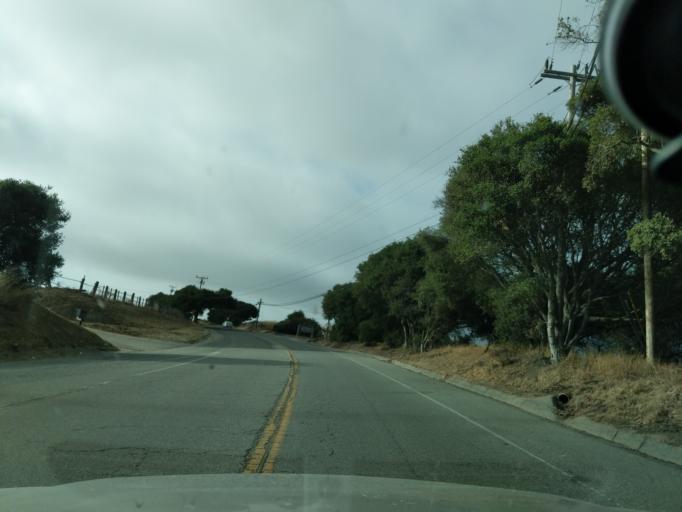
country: US
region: California
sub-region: Monterey County
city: Elkhorn
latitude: 36.7962
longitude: -121.7203
